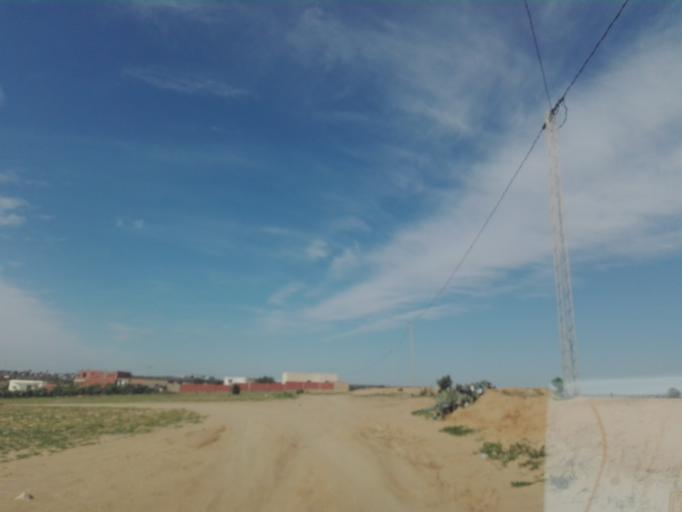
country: TN
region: Safaqis
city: Sfax
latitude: 34.7423
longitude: 10.5070
